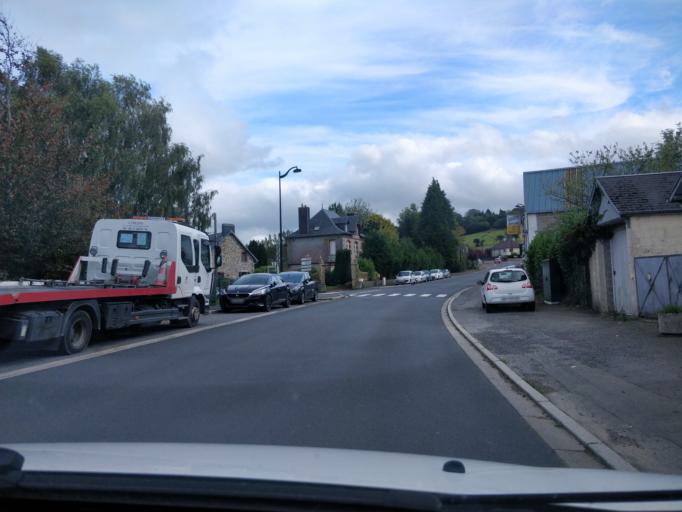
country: FR
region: Lower Normandy
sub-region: Departement du Calvados
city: Saint-Sever-Calvados
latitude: 48.8403
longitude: -1.0426
